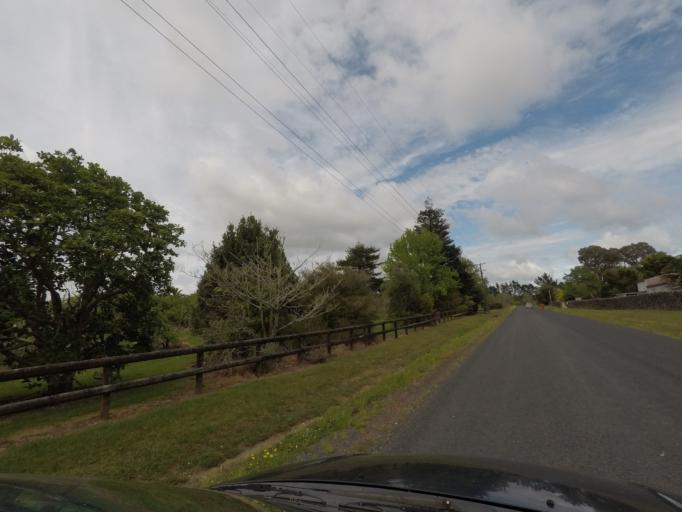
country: NZ
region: Auckland
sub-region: Auckland
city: Rosebank
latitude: -36.7762
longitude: 174.5953
